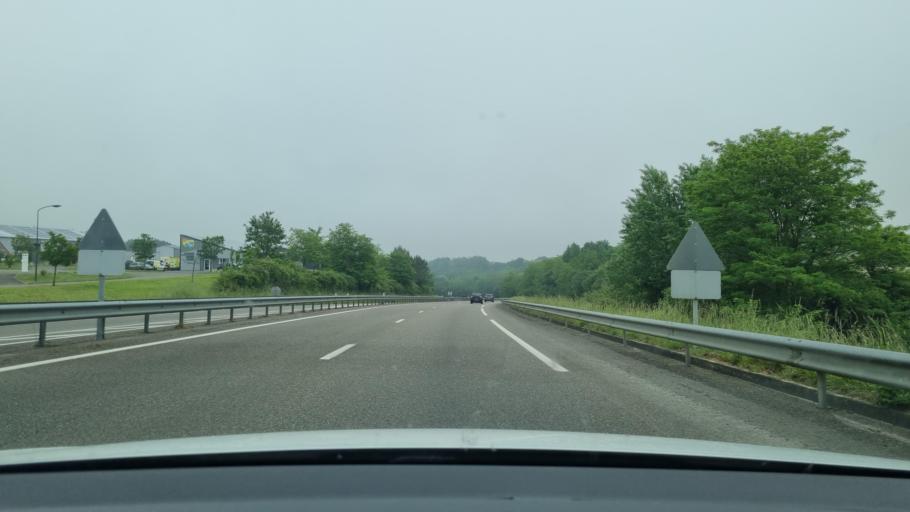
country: FR
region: Aquitaine
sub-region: Departement des Landes
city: Saint-Sever
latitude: 43.7484
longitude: -0.5600
